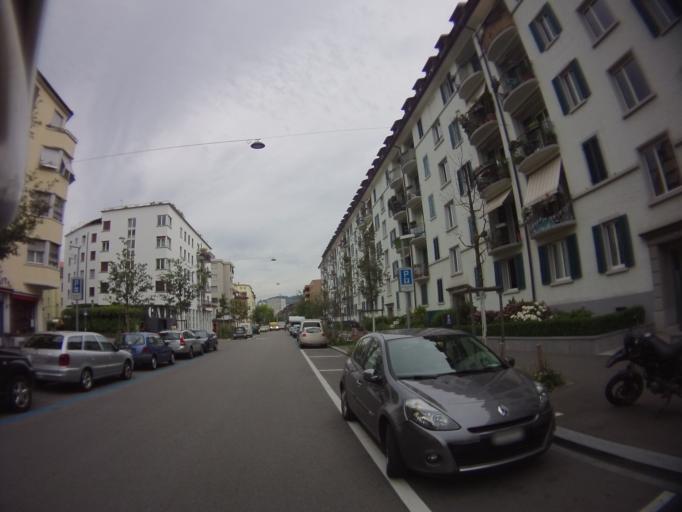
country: CH
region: Zurich
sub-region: Bezirk Zuerich
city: Aussersihl
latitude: 47.3773
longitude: 8.5164
